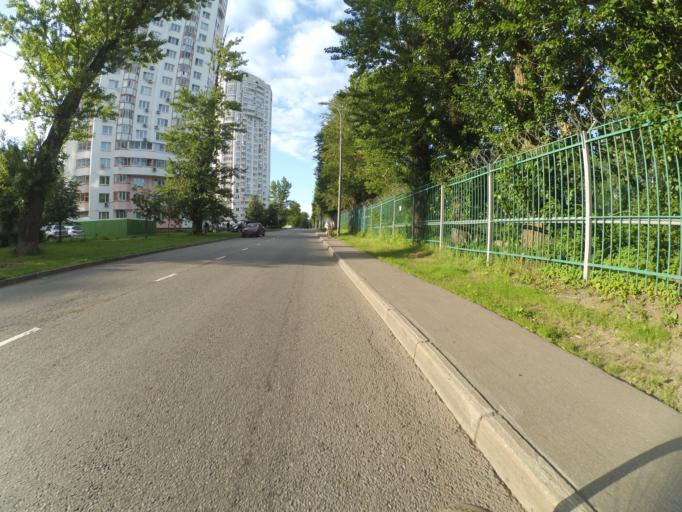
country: RU
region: Moscow
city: Pokrovskoye-Streshnevo
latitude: 55.8305
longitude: 37.4590
